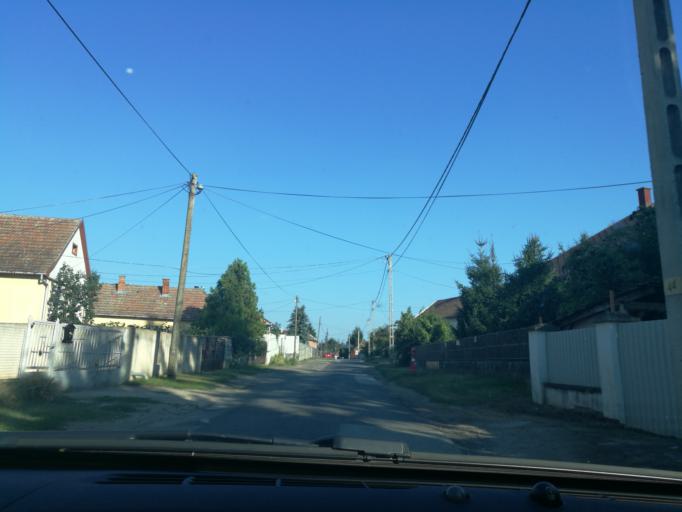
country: HU
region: Szabolcs-Szatmar-Bereg
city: Tiszabercel
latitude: 48.1661
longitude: 21.5885
